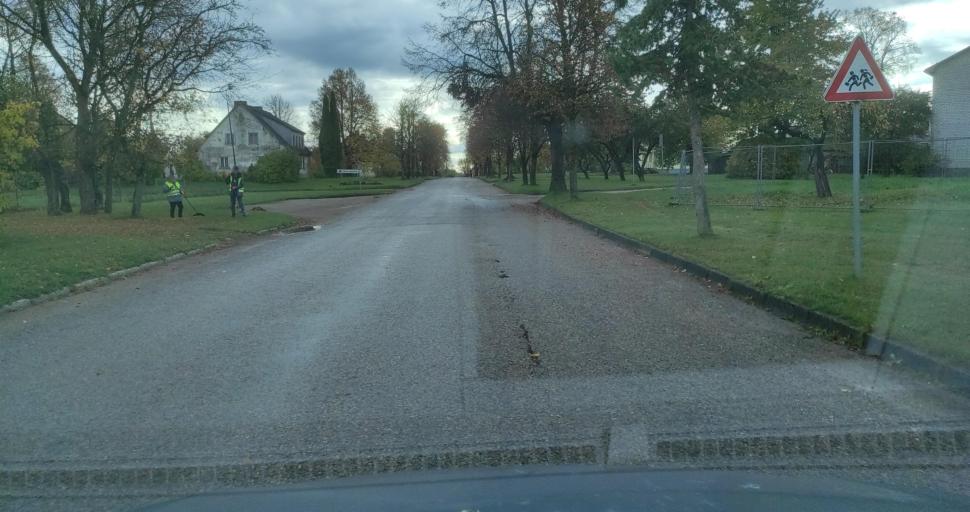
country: LV
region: Vainode
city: Vainode
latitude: 56.5710
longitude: 21.8972
